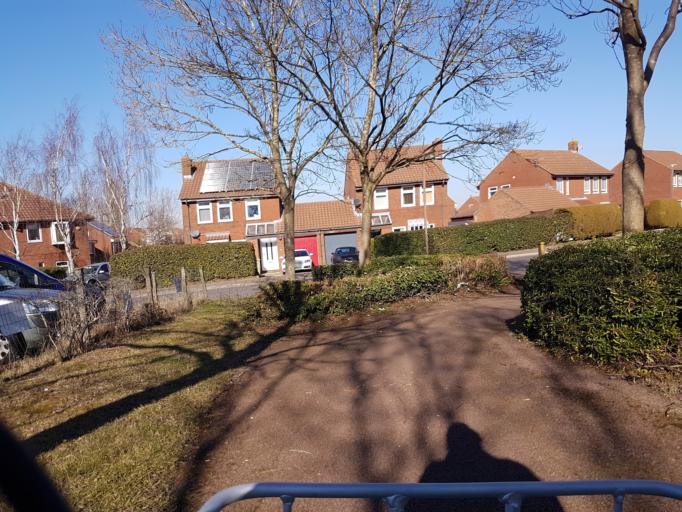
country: GB
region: England
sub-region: Buckinghamshire
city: Newton Longville
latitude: 51.9997
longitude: -0.7735
